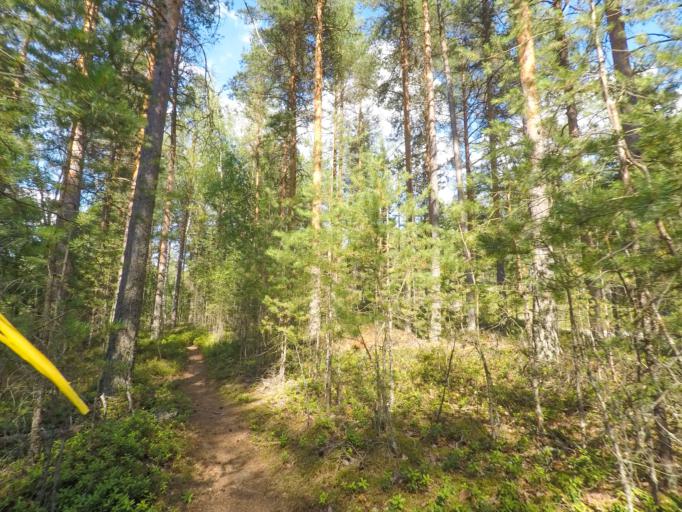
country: FI
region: Southern Savonia
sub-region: Mikkeli
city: Puumala
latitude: 61.4924
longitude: 28.1669
